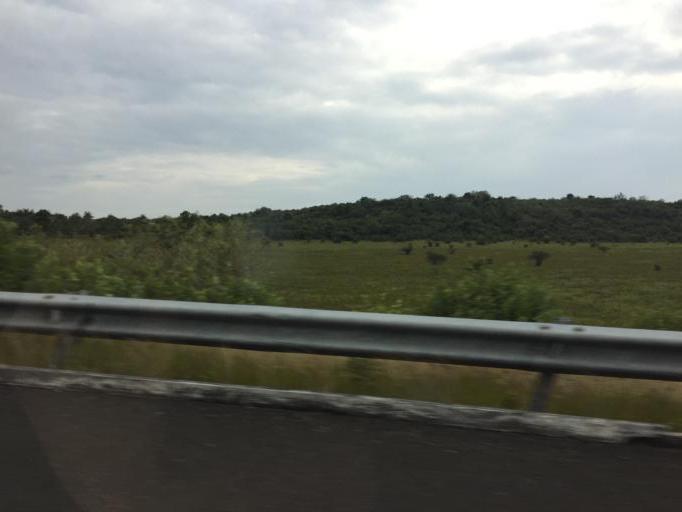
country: MX
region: Michoacan
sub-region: Puruandiro
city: San Lorenzo
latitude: 19.9441
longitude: -101.6334
